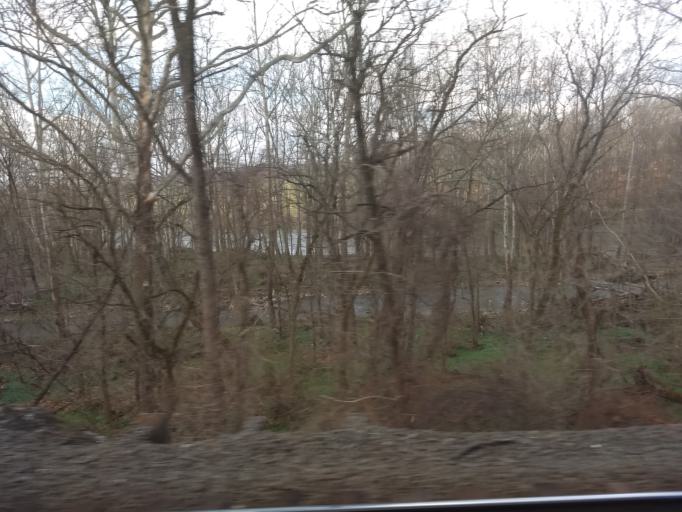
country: US
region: Pennsylvania
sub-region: Huntingdon County
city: Huntingdon
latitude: 40.4988
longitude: -78.0241
